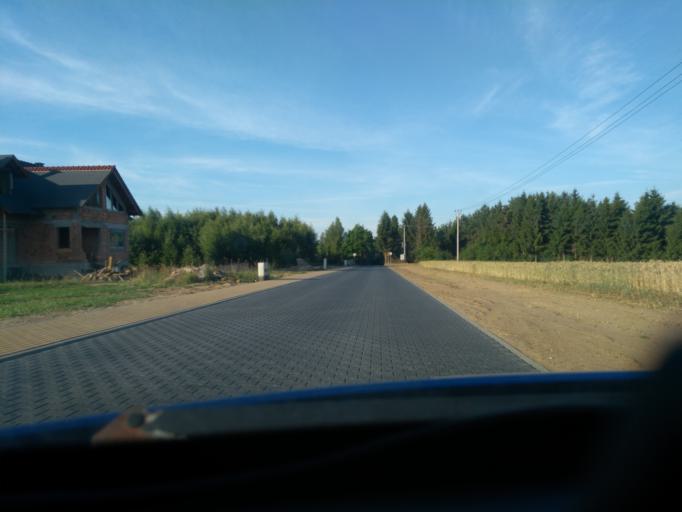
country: PL
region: Pomeranian Voivodeship
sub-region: Powiat kartuski
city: Przodkowo
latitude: 54.3859
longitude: 18.3188
